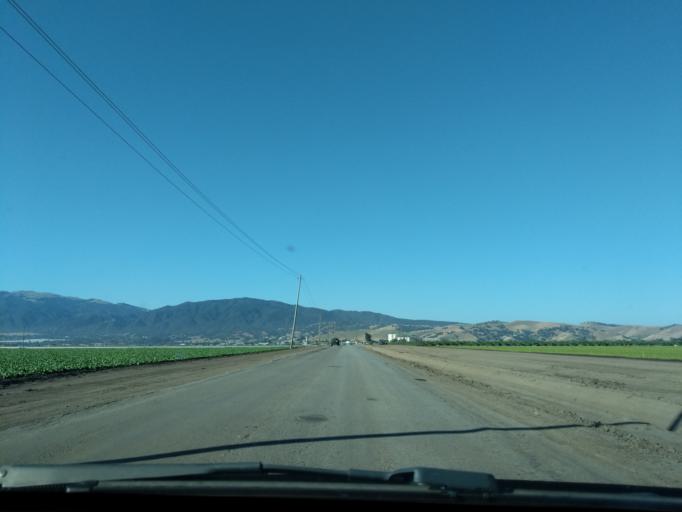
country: US
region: California
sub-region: Monterey County
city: Salinas
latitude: 36.6414
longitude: -121.6359
